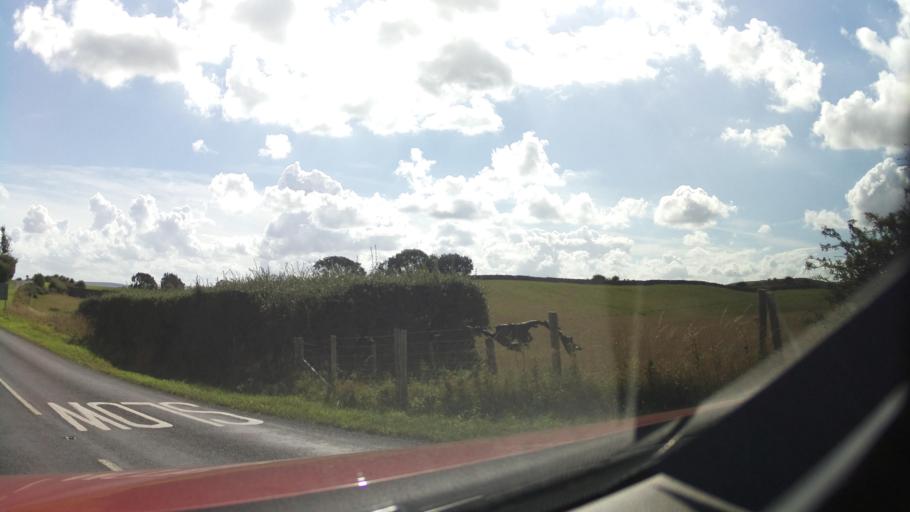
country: GB
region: England
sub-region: North Yorkshire
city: Leyburn
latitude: 54.3417
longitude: -1.8202
